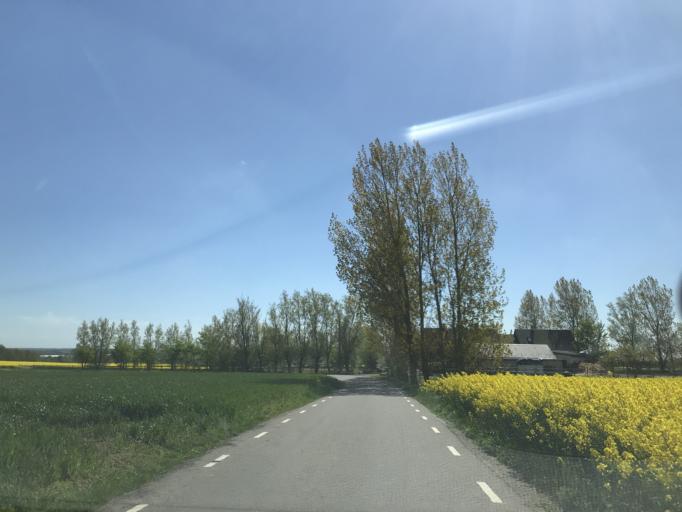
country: SE
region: Skane
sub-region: Landskrona
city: Asmundtorp
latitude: 55.9016
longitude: 12.9230
